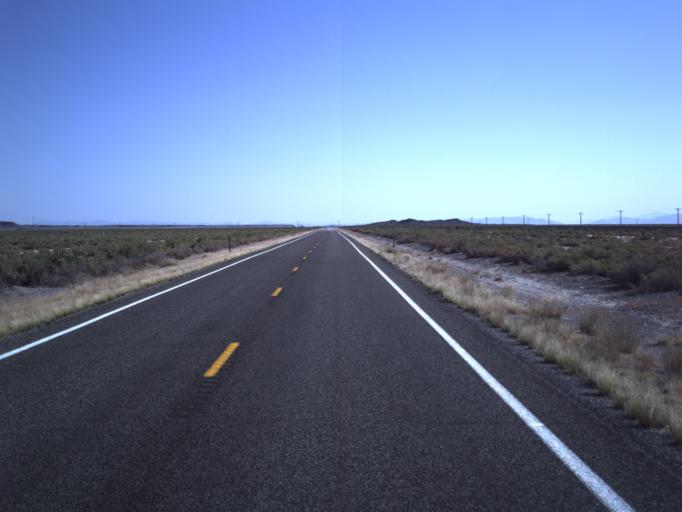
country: US
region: Utah
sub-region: Millard County
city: Delta
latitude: 39.1230
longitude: -112.7366
